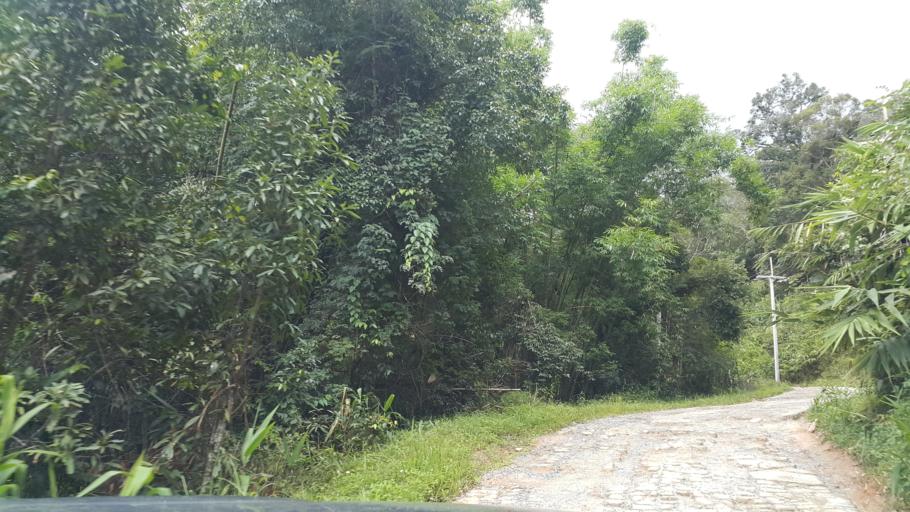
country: TH
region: Lampang
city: Wang Nuea
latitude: 19.1016
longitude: 99.3676
